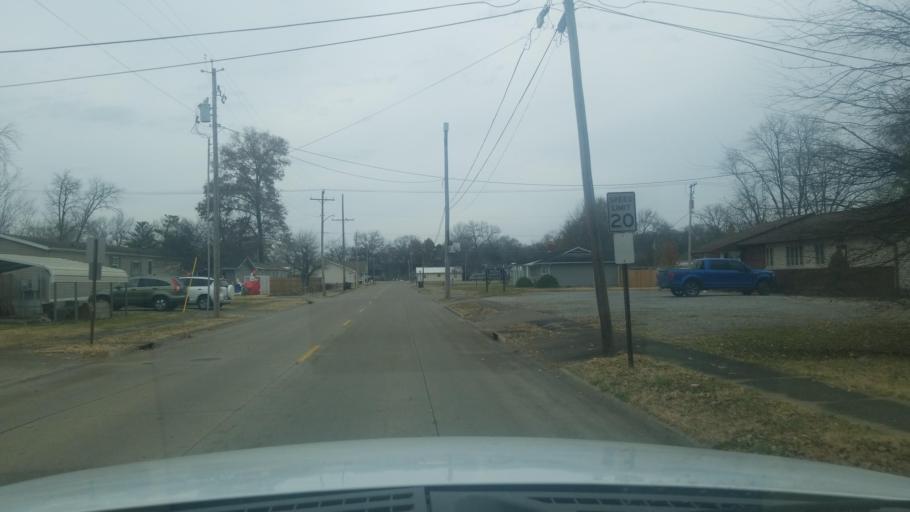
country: US
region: Illinois
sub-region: Saline County
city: Harrisburg
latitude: 37.7365
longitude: -88.5524
